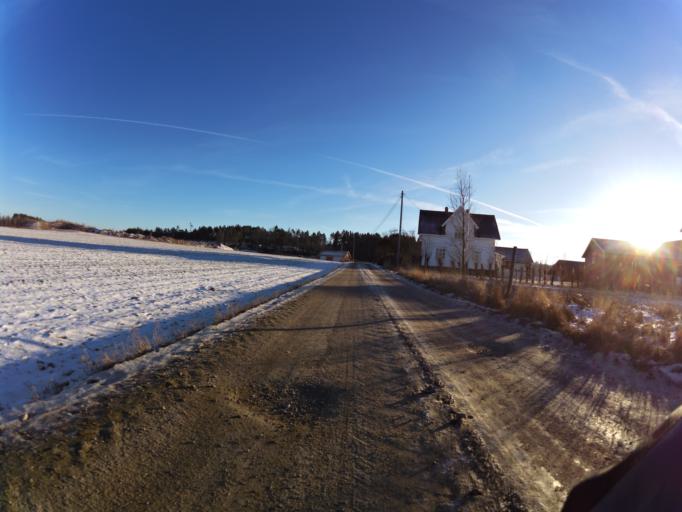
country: NO
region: Ostfold
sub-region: Fredrikstad
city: Lervik
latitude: 59.2454
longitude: 10.8117
